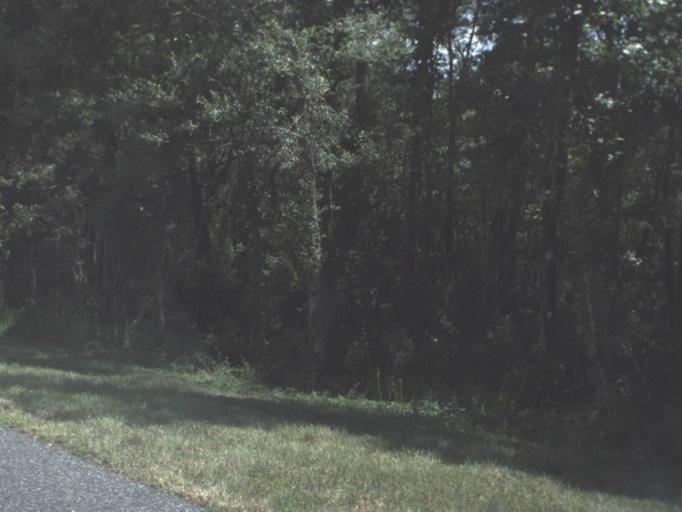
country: US
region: Florida
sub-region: Taylor County
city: Perry
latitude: 29.9304
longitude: -83.4440
